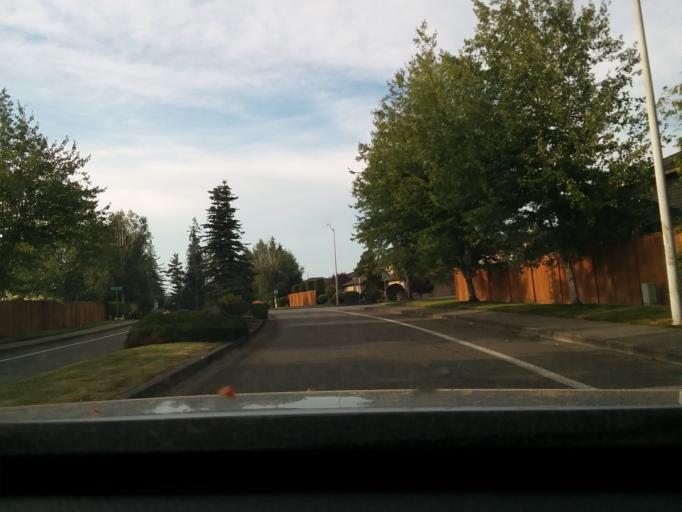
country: US
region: Washington
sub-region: Snohomish County
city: Silver Firs
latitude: 47.8560
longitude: -122.1401
